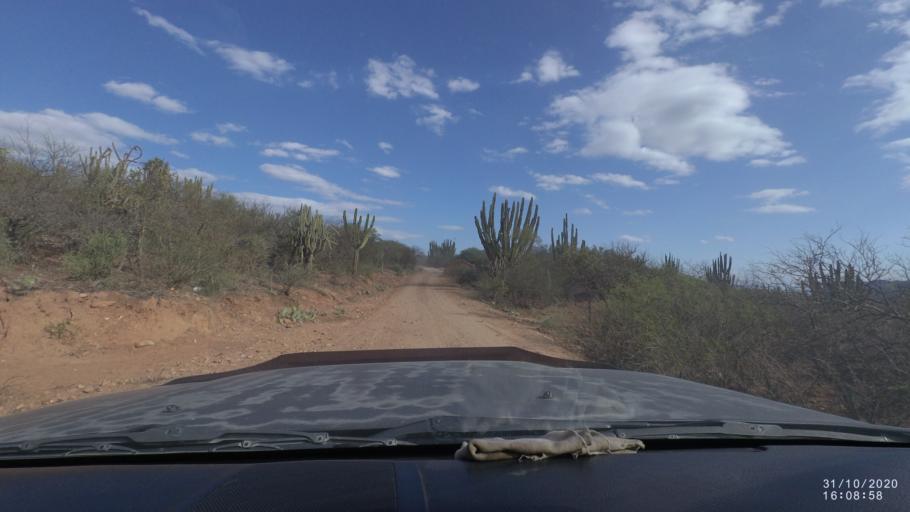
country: BO
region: Chuquisaca
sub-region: Provincia Zudanez
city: Mojocoya
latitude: -18.3861
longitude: -64.6387
